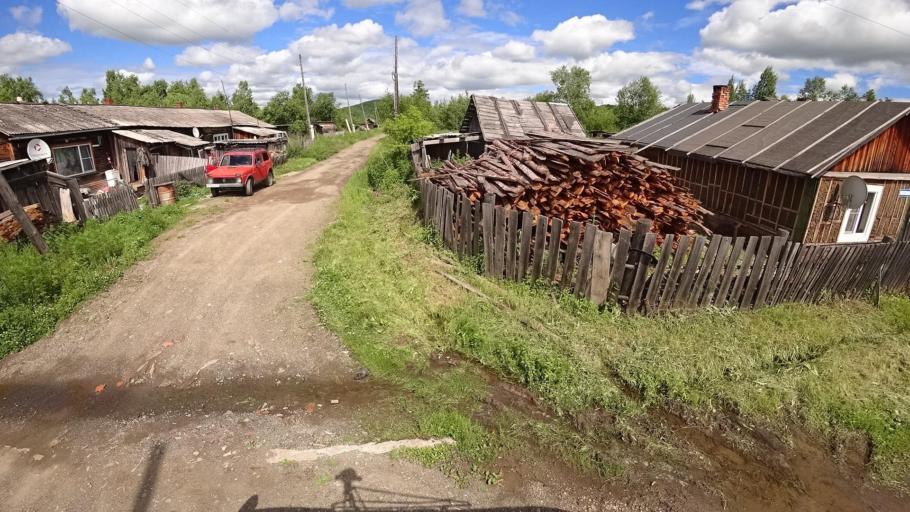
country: RU
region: Khabarovsk Krai
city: Litovko
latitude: 49.3681
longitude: 135.1684
